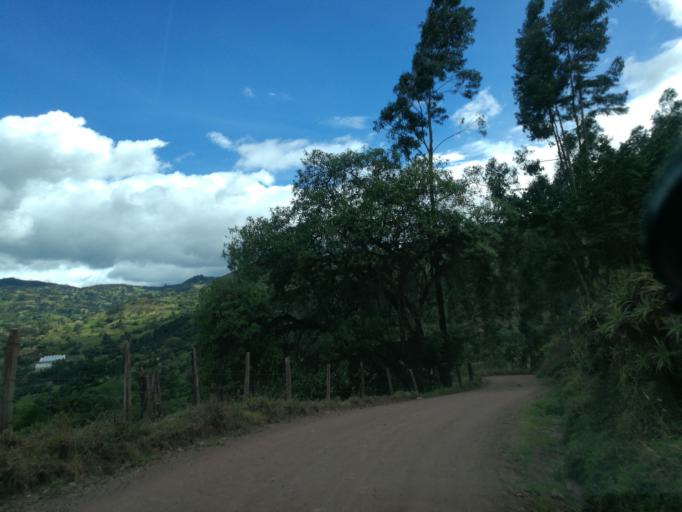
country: CO
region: Boyaca
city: Susacon
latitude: 6.1209
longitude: -72.7131
